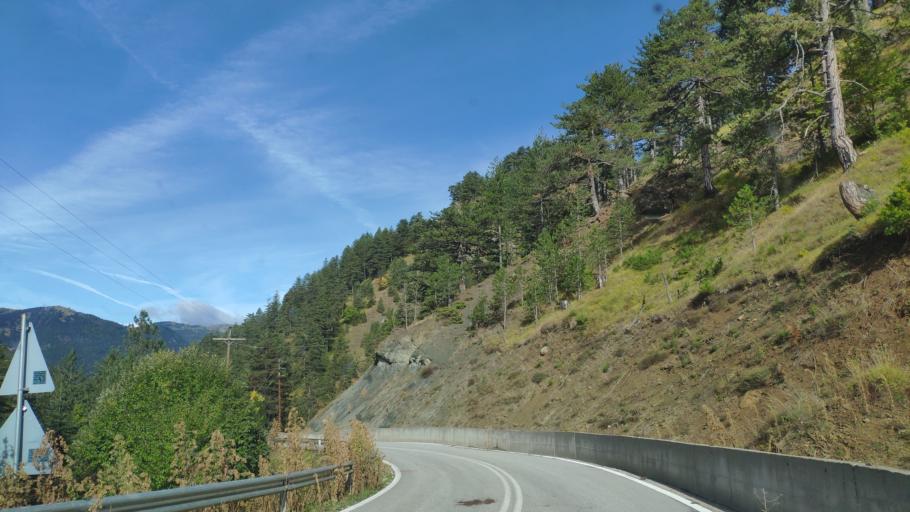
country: AL
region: Korce
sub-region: Rrethi i Devollit
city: Miras
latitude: 40.3978
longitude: 20.9025
